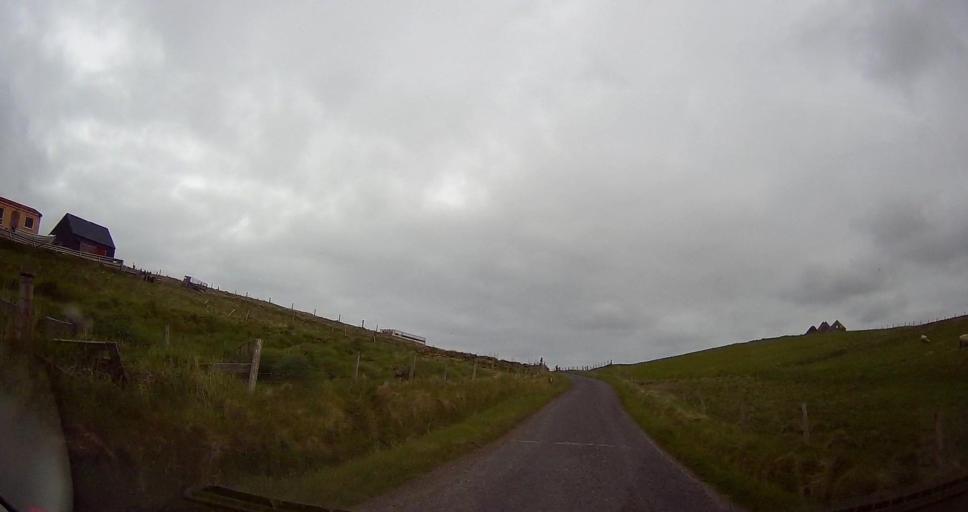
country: GB
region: Scotland
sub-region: Shetland Islands
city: Shetland
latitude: 60.8010
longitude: -0.8758
